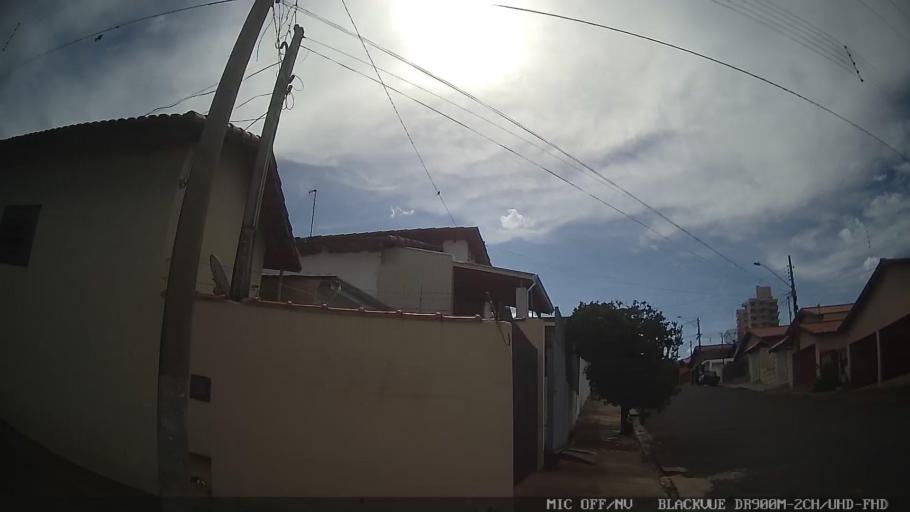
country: BR
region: Sao Paulo
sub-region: Conchas
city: Conchas
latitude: -23.0136
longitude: -48.0035
